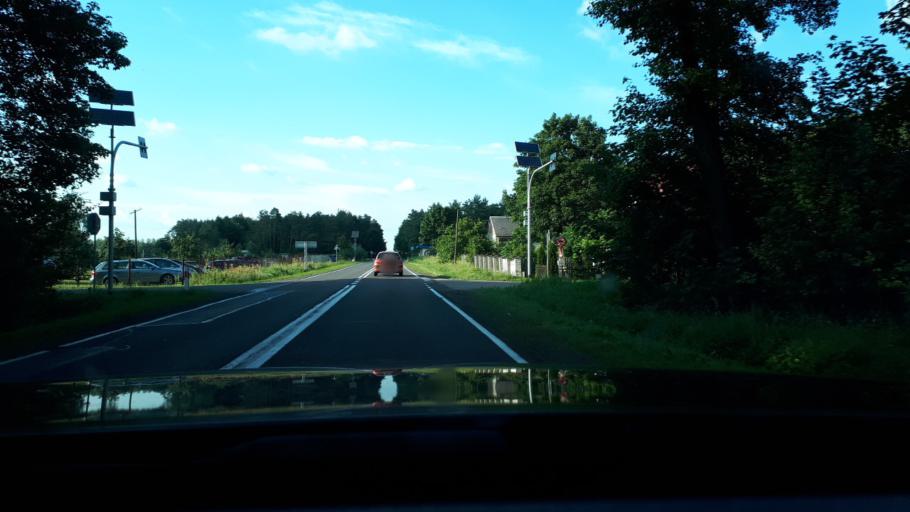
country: PL
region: Masovian Voivodeship
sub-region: Powiat plonski
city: Sochocin
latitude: 52.6710
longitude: 20.4554
